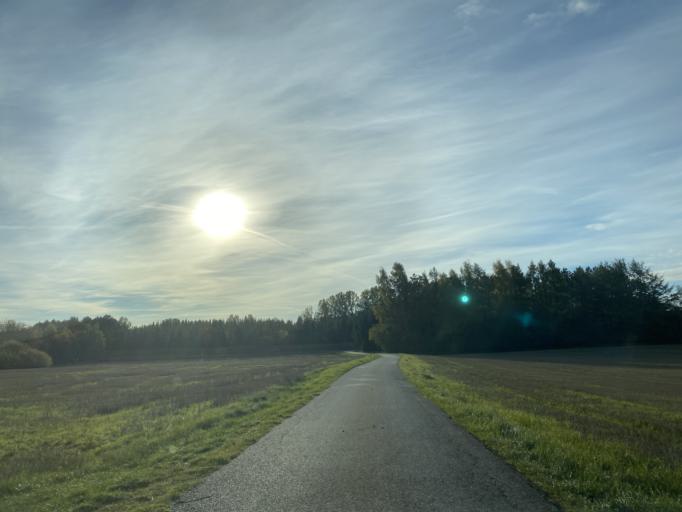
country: DK
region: Capital Region
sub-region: Egedal Kommune
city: Ganlose
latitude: 55.8101
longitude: 12.2883
